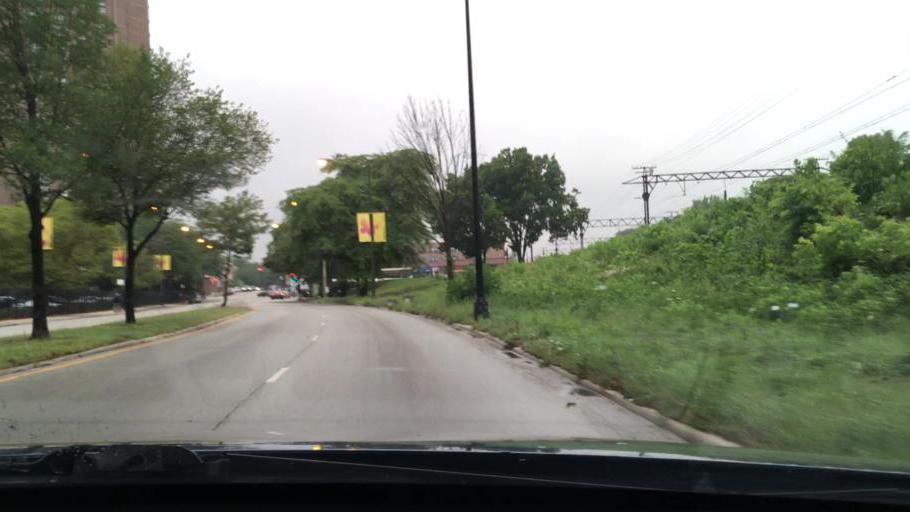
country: US
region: Illinois
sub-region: Cook County
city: Chicago
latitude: 41.8083
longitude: -87.5908
